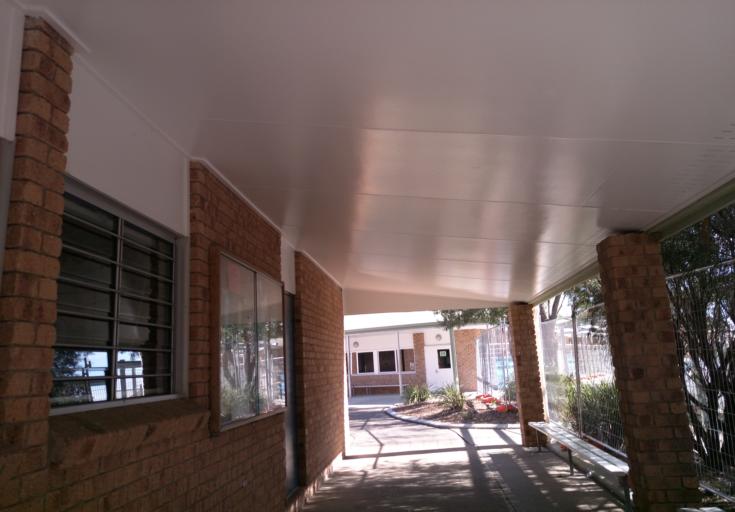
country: AU
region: Queensland
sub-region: Logan
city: Waterford West
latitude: -27.7084
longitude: 153.1492
